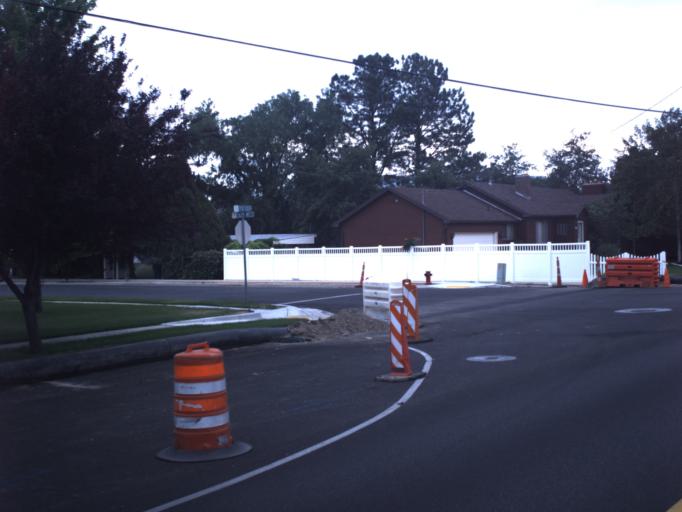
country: US
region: Utah
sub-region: Davis County
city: Syracuse
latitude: 41.0892
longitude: -112.0772
